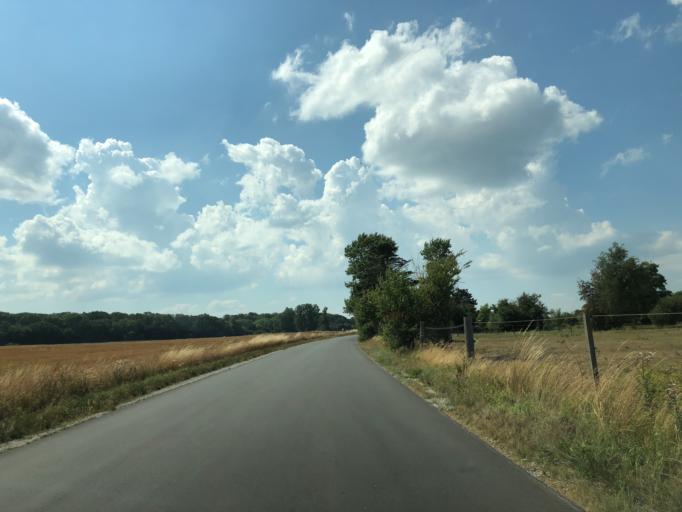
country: DK
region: Capital Region
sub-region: Halsnaes Kommune
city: Hundested
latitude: 55.9785
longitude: 11.8842
